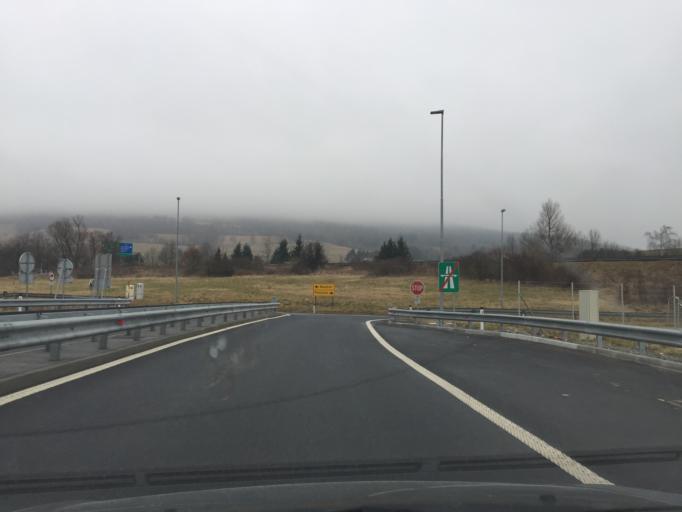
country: SI
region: Divaca
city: Divaca
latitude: 45.7586
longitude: 14.0738
